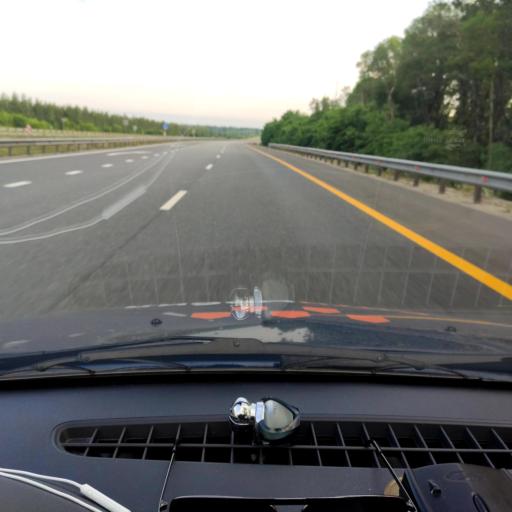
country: RU
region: Lipetsk
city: Zadonsk
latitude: 52.4707
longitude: 38.7684
